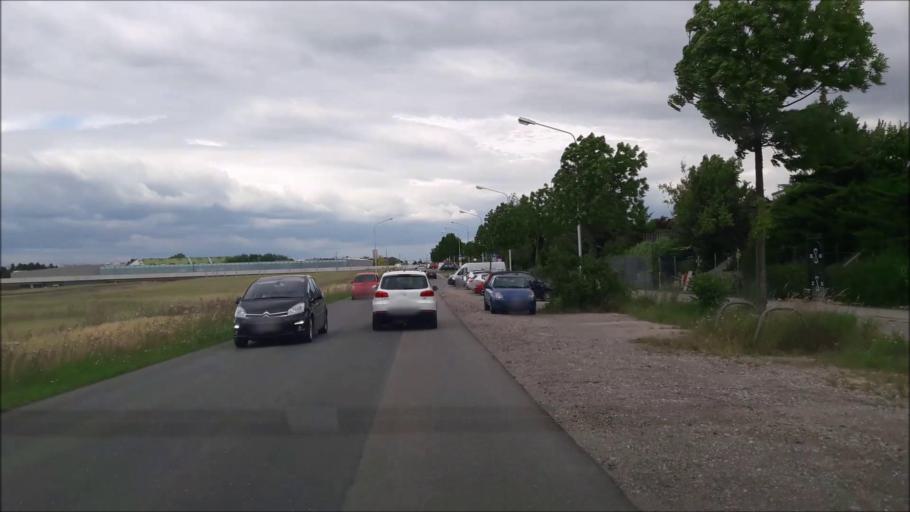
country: AT
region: Lower Austria
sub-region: Politischer Bezirk Wien-Umgebung
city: Gerasdorf bei Wien
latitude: 48.2293
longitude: 16.4855
